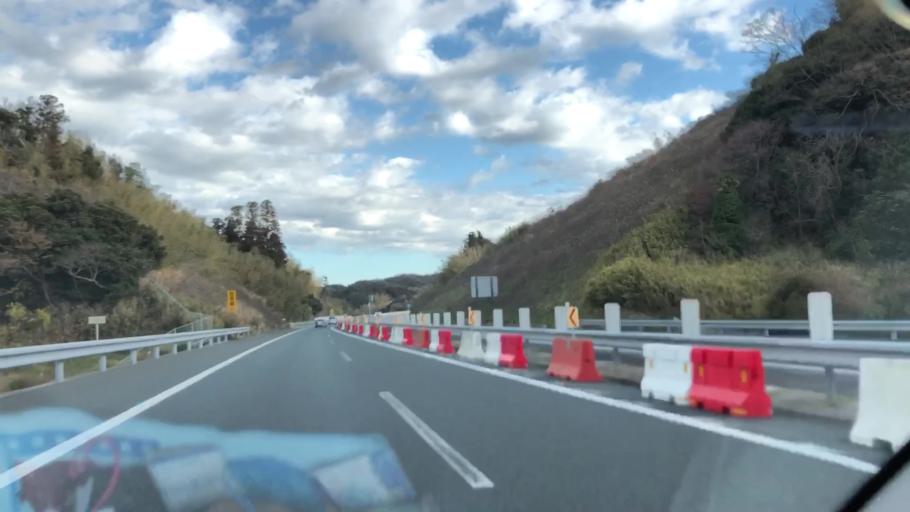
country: JP
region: Chiba
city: Kimitsu
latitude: 35.2580
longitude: 139.8948
